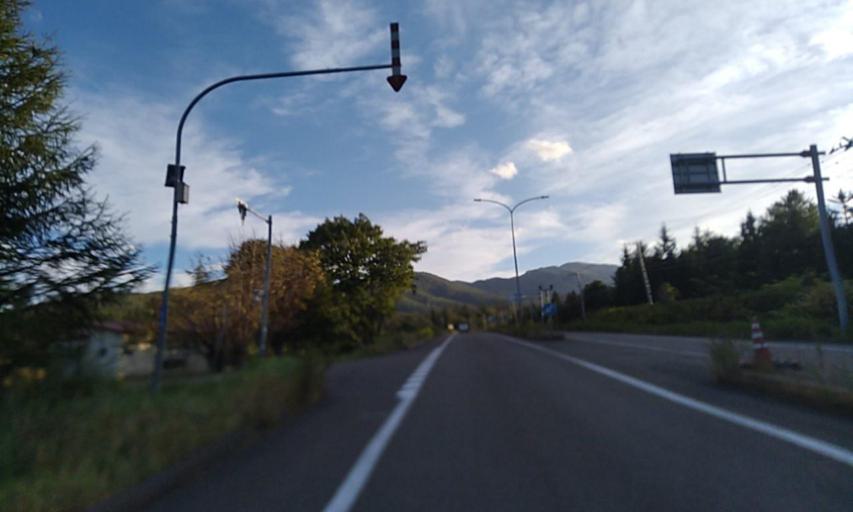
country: JP
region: Hokkaido
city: Otofuke
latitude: 42.9865
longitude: 142.8392
